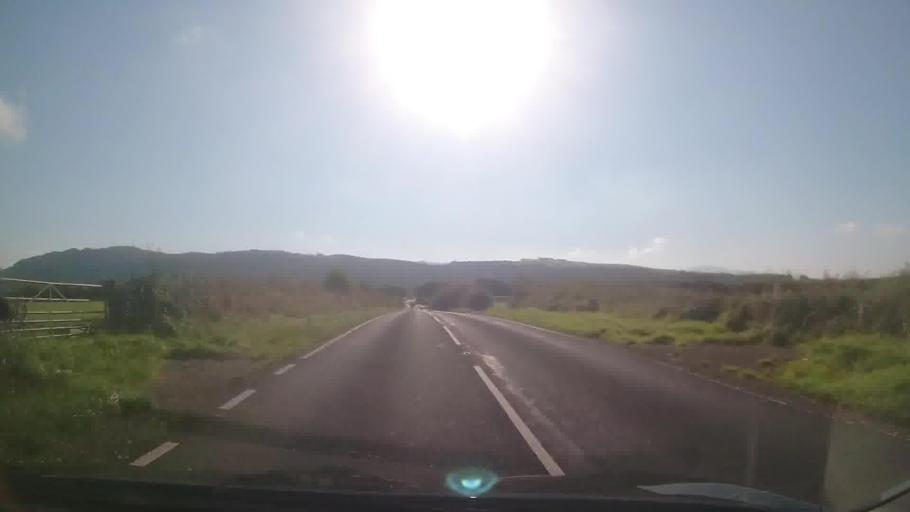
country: GB
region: England
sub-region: Cumbria
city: Seascale
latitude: 54.3739
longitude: -3.4093
